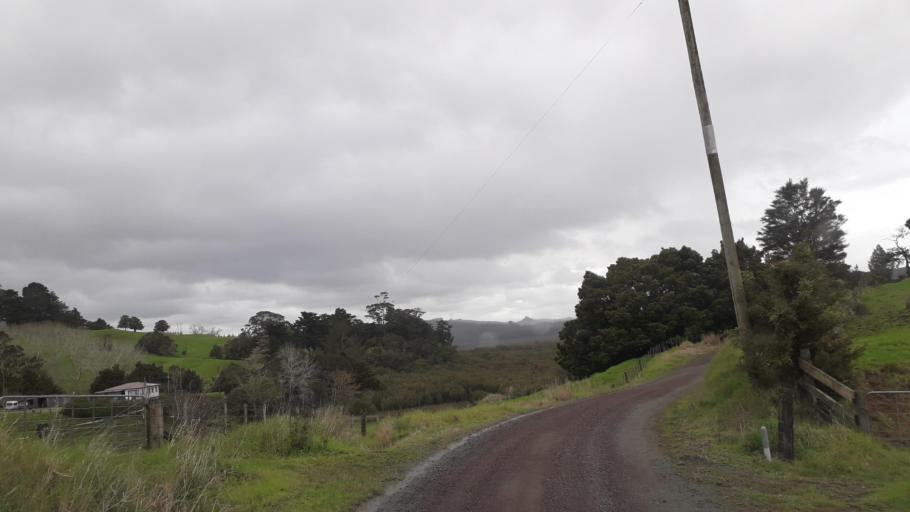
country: NZ
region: Northland
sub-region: Far North District
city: Waimate North
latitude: -35.3124
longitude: 173.5652
